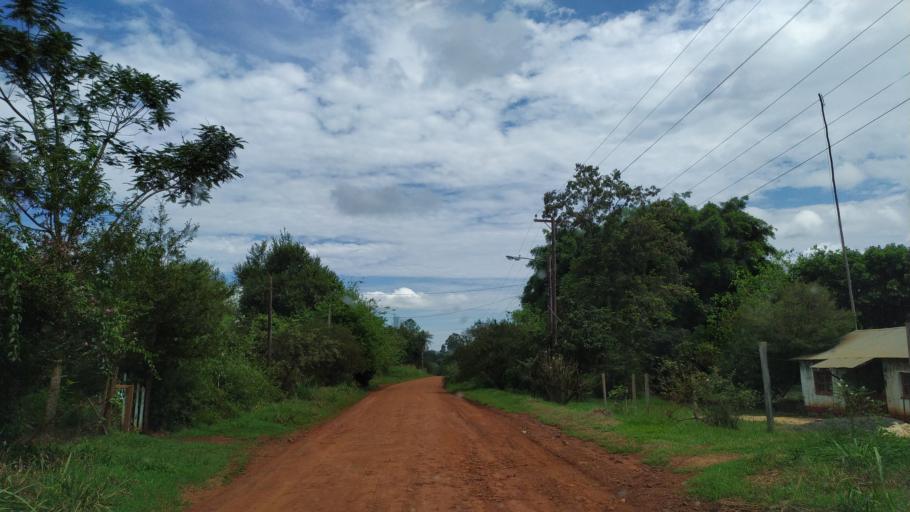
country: AR
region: Misiones
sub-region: Departamento de Eldorado
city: Eldorado
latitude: -26.5174
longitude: -54.5930
